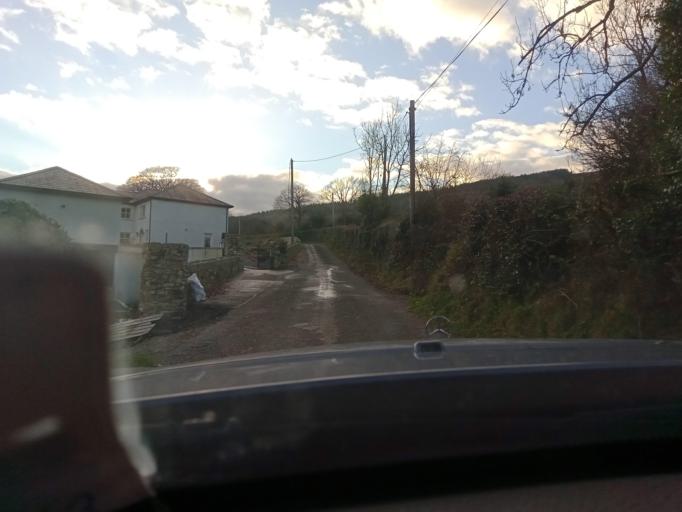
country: IE
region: Leinster
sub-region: Kilkenny
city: Graiguenamanagh
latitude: 52.5035
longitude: -6.9422
